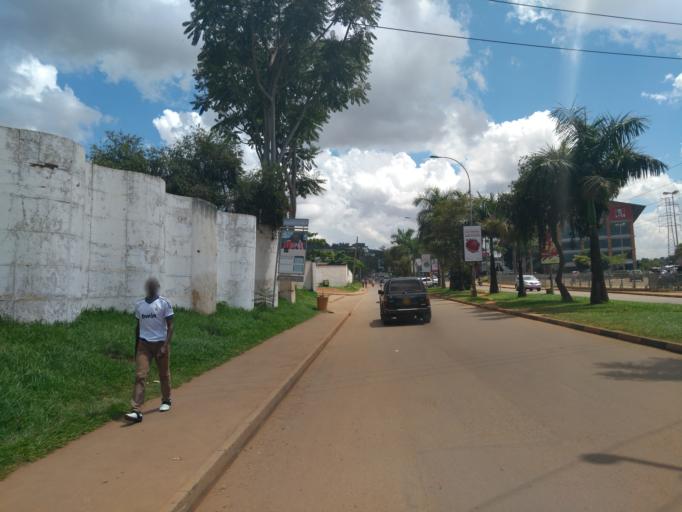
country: UG
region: Central Region
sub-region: Kampala District
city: Kampala
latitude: 0.3258
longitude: 32.6061
